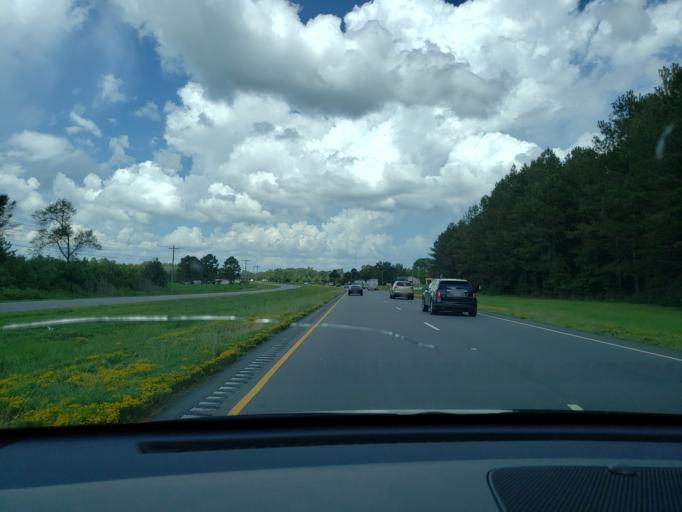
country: US
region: North Carolina
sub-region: Robeson County
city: Saint Pauls
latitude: 34.7802
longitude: -78.8107
